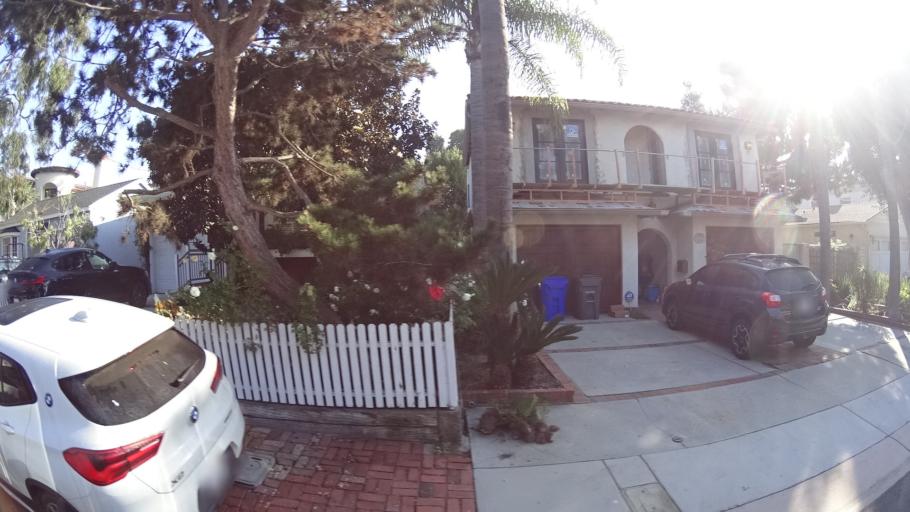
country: US
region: California
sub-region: Los Angeles County
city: Manhattan Beach
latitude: 33.8893
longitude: -118.3978
